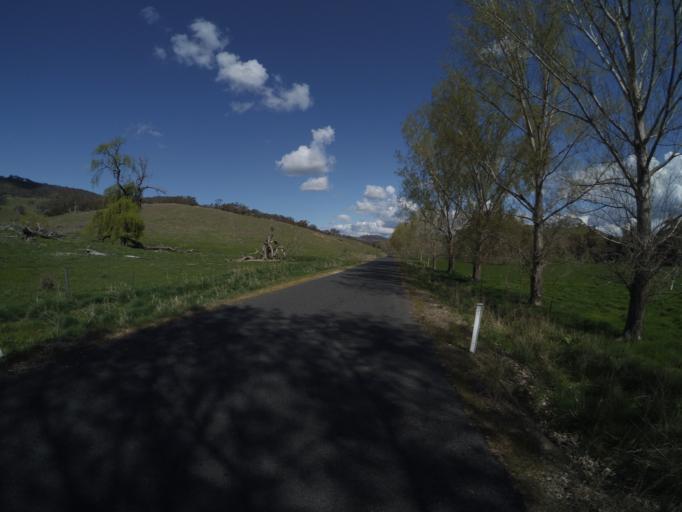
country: AU
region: New South Wales
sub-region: Yass Valley
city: Murrumbateman
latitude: -35.0394
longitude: 148.8403
